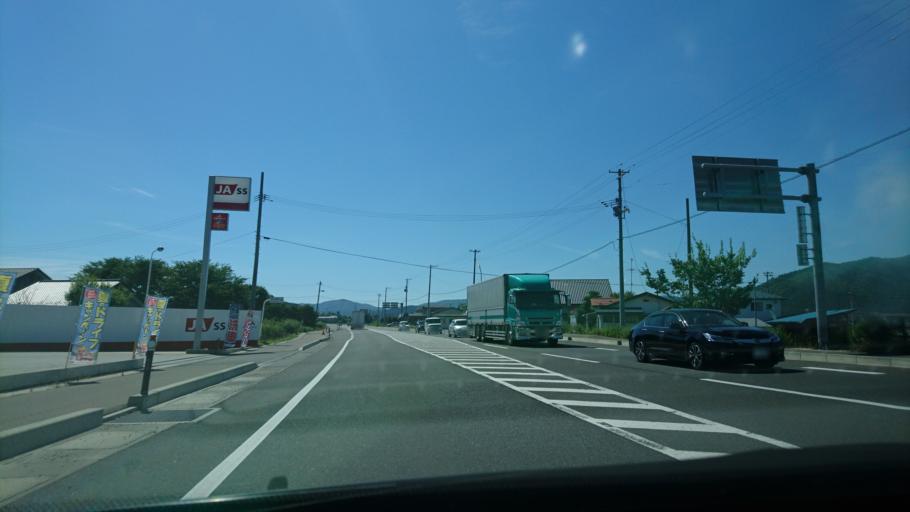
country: JP
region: Iwate
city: Tono
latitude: 39.3116
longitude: 141.5704
